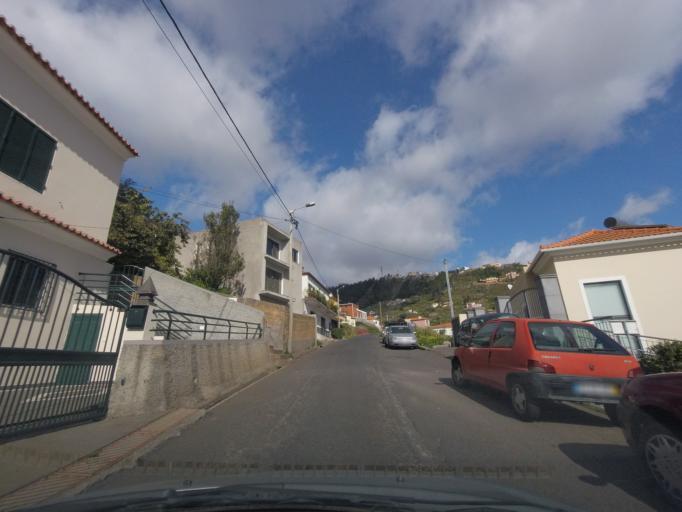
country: PT
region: Madeira
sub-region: Ribeira Brava
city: Campanario
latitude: 32.6620
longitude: -17.0105
